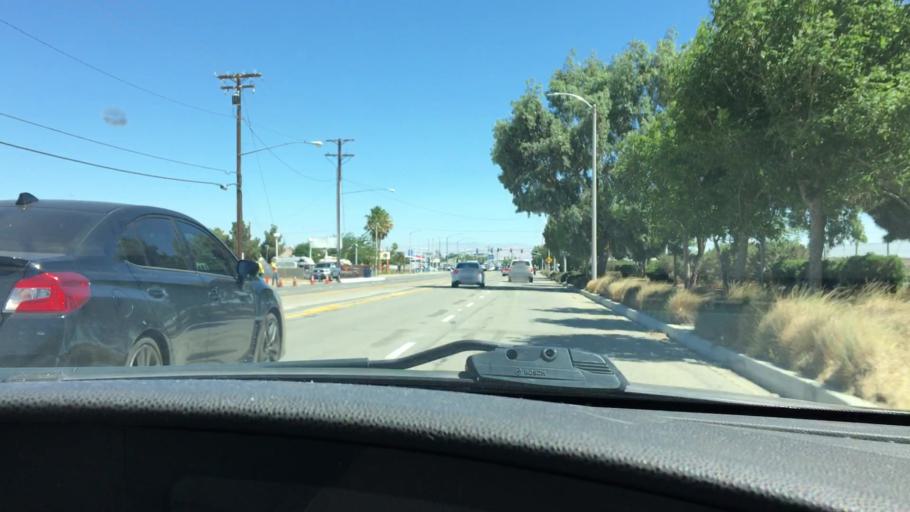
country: US
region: California
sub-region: Los Angeles County
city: Lancaster
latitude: 34.6725
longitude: -118.1324
